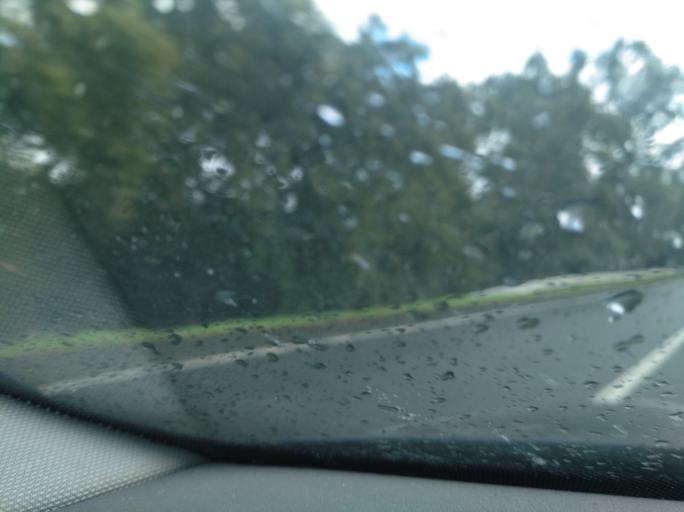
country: PT
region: Setubal
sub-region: Grandola
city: Grandola
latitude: 38.0697
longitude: -8.4144
